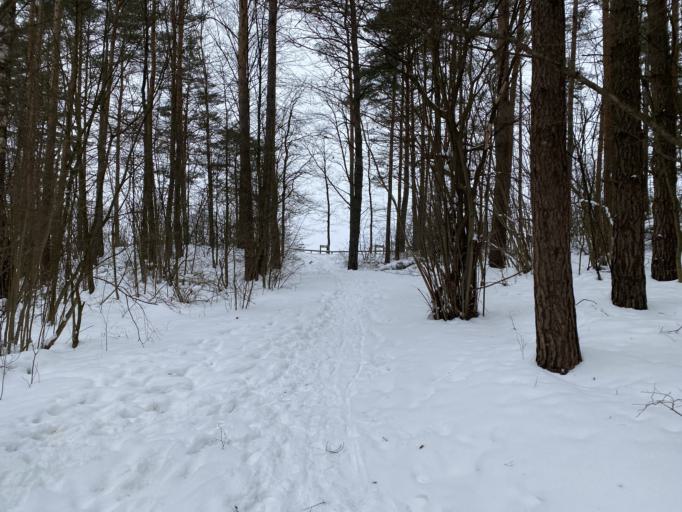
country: LT
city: Ramuciai
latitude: 54.8828
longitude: 24.0621
